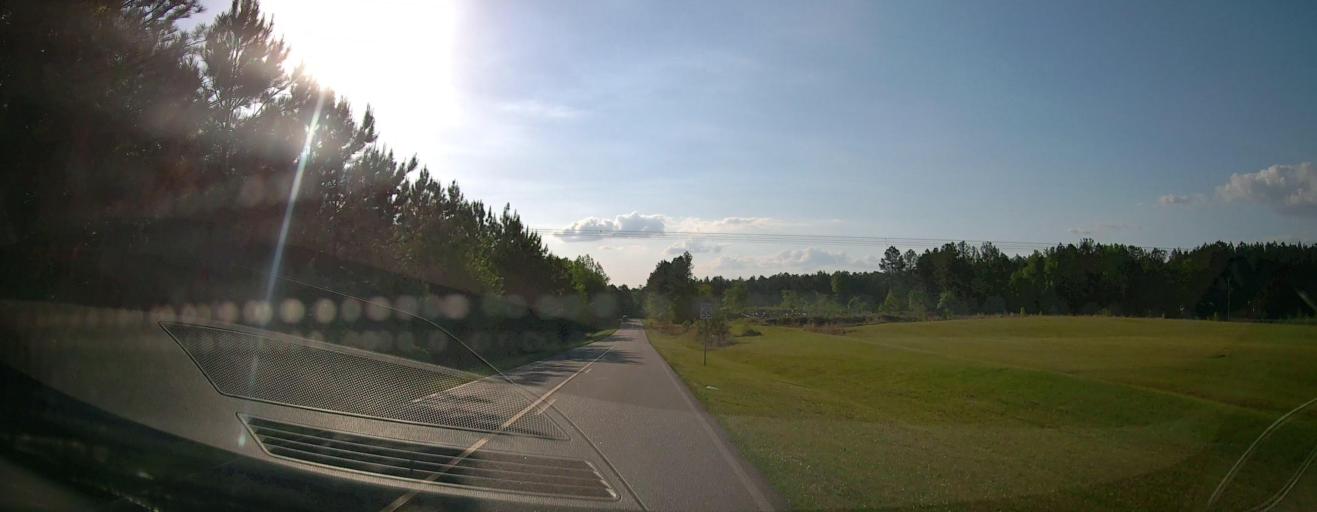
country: US
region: Georgia
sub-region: Putnam County
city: Eatonton
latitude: 33.2725
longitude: -83.3036
